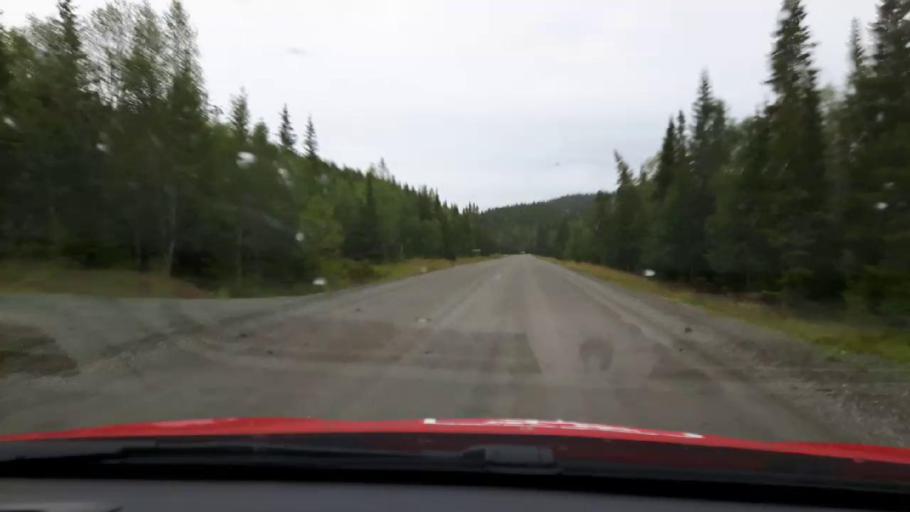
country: SE
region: Jaemtland
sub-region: Are Kommun
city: Are
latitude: 63.4265
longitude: 12.7395
